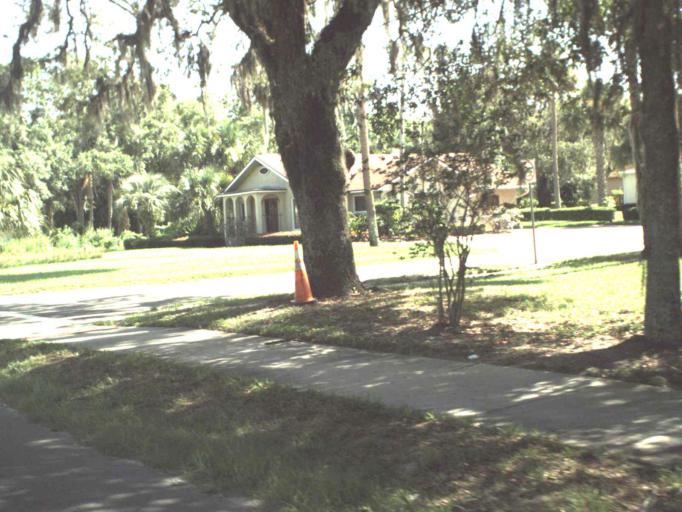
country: US
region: Florida
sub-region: Seminole County
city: Oviedo
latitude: 28.6686
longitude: -81.2085
